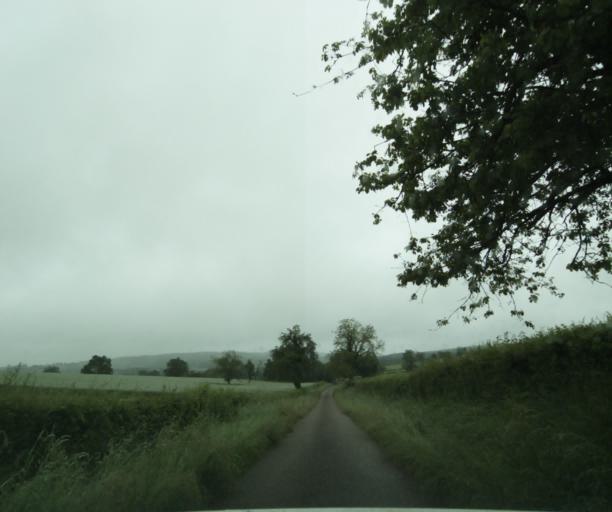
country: FR
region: Bourgogne
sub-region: Departement de Saone-et-Loire
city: Charolles
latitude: 46.4467
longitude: 4.3968
